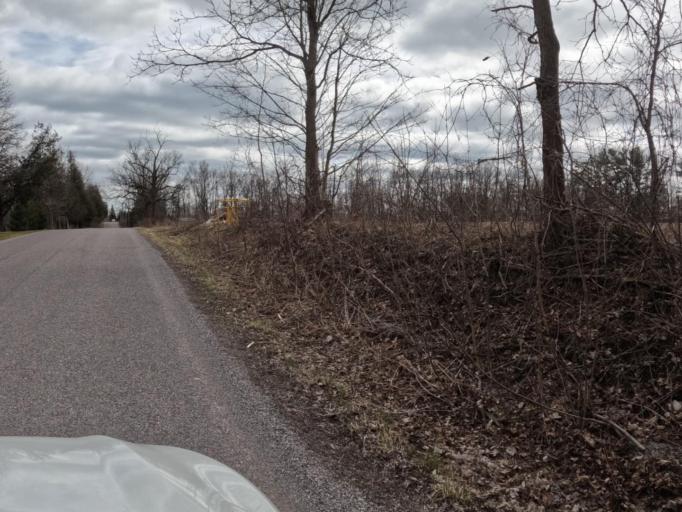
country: CA
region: Ontario
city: Norfolk County
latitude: 42.8065
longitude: -80.2156
